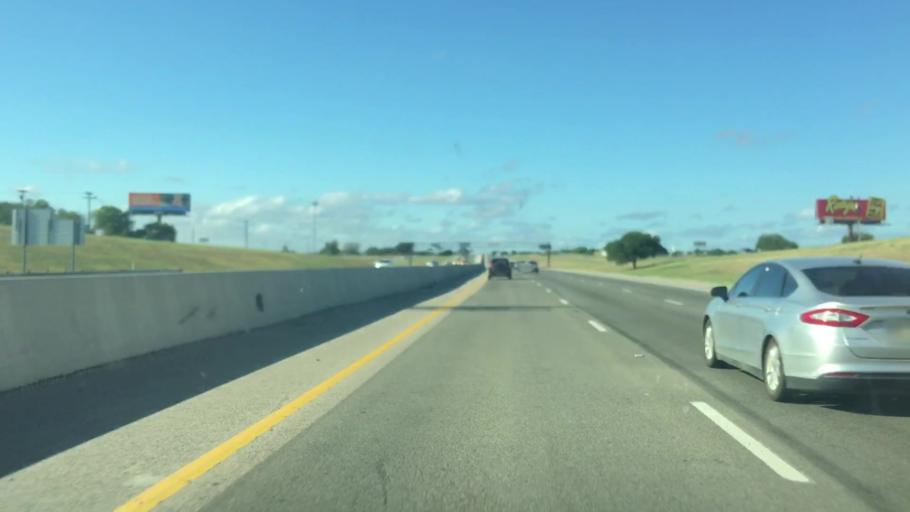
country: US
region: Texas
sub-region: Williamson County
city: Serenada
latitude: 30.8060
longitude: -97.6154
